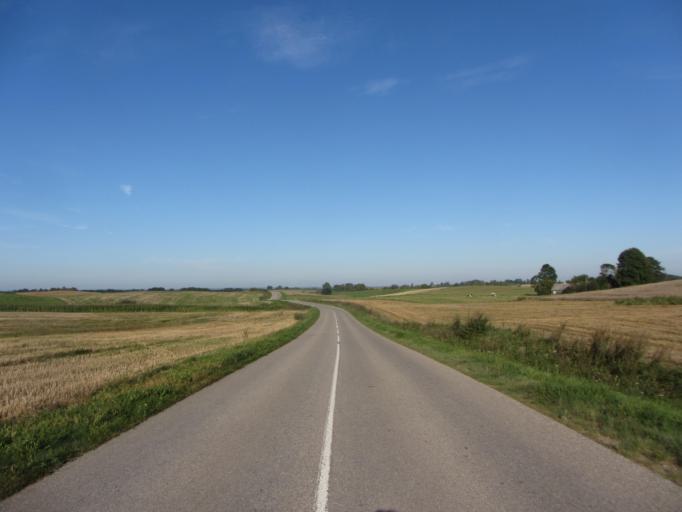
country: LT
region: Alytaus apskritis
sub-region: Alytus
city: Alytus
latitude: 54.3276
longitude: 23.8752
